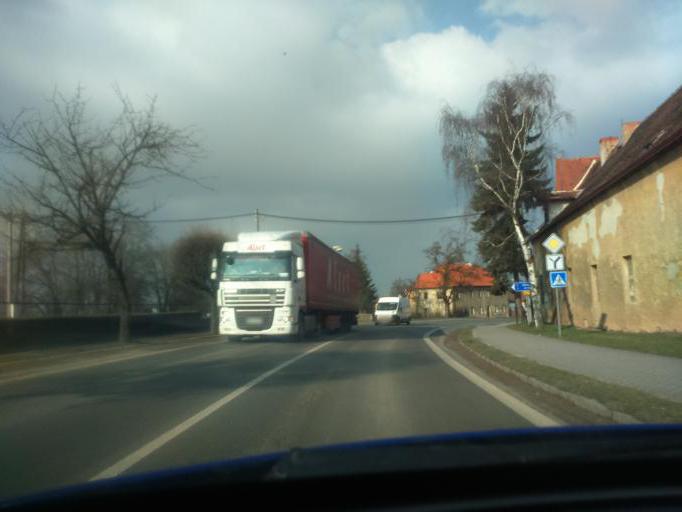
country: CZ
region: Plzensky
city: Chotesov
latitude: 49.6538
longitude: 13.1967
